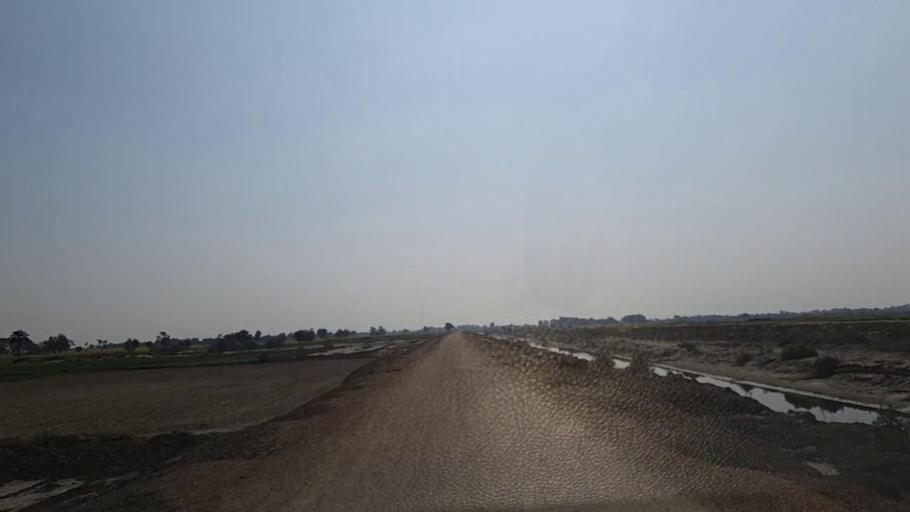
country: PK
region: Sindh
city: Nawabshah
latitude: 26.2635
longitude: 68.5030
